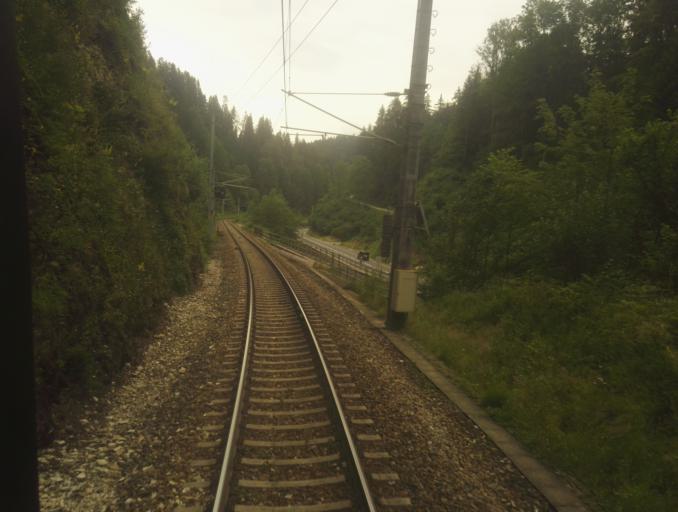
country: AT
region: Salzburg
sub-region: Politischer Bezirk Sankt Johann im Pongau
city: Huttau
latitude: 47.4291
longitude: 13.2778
